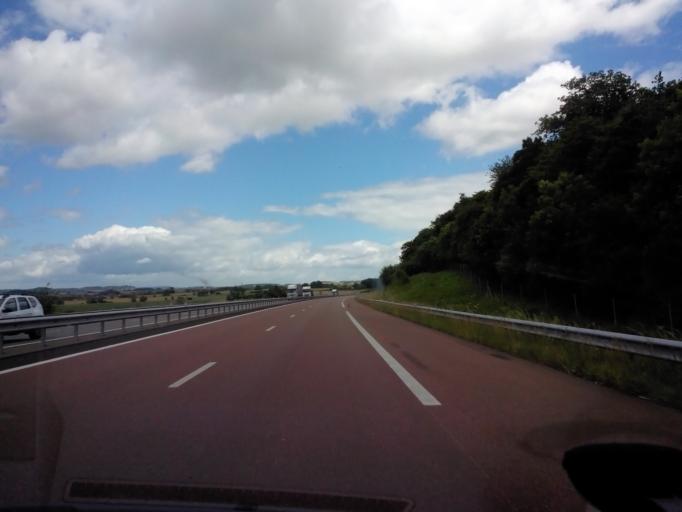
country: FR
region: Champagne-Ardenne
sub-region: Departement de la Haute-Marne
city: Saulxures
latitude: 48.0731
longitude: 5.5988
